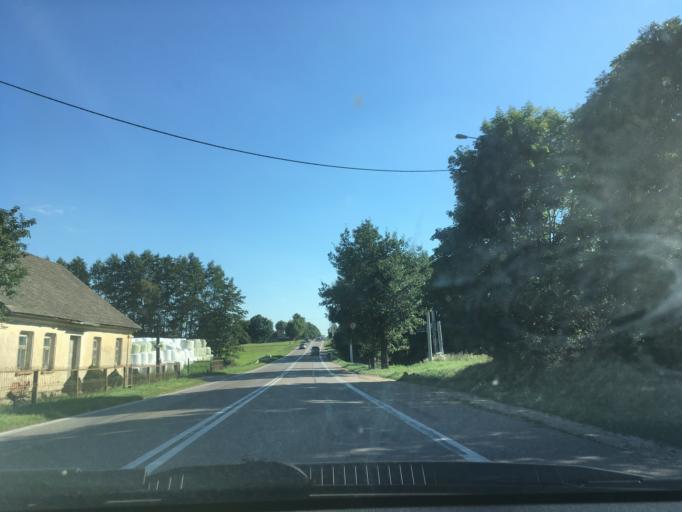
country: PL
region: Podlasie
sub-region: Powiat sokolski
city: Suchowola
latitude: 53.4844
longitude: 23.0935
